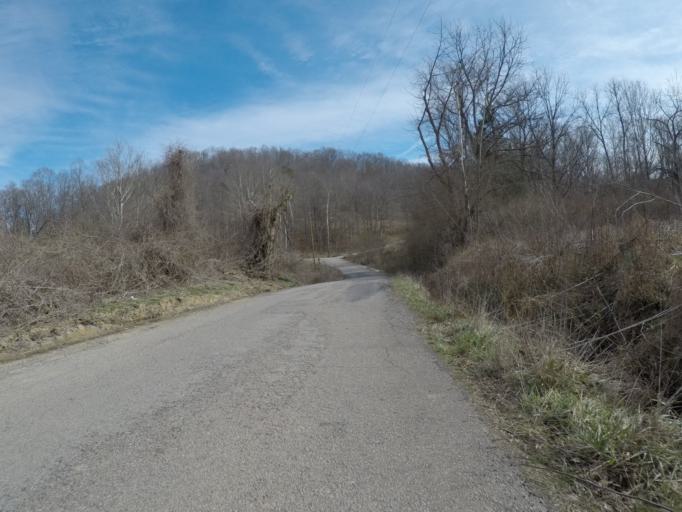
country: US
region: West Virginia
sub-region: Wayne County
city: Lavalette
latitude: 38.3374
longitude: -82.5014
